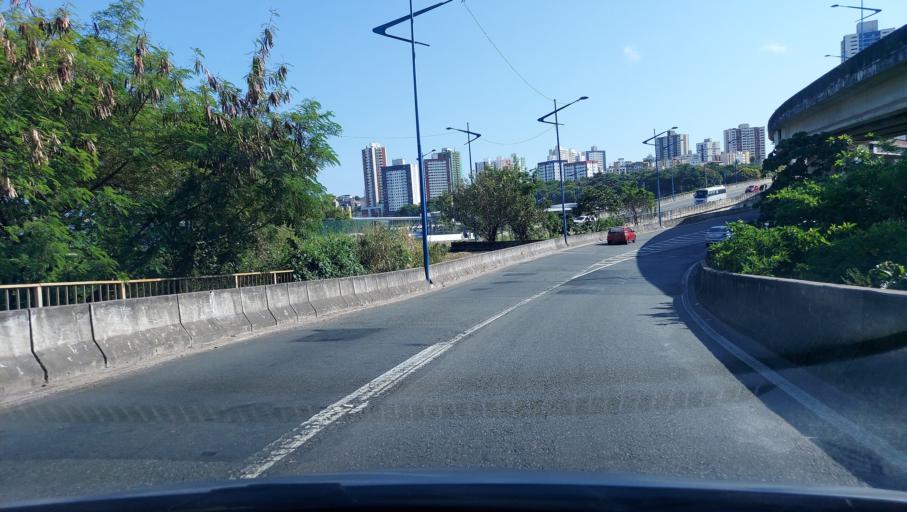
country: BR
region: Bahia
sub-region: Salvador
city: Salvador
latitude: -12.9674
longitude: -38.4776
